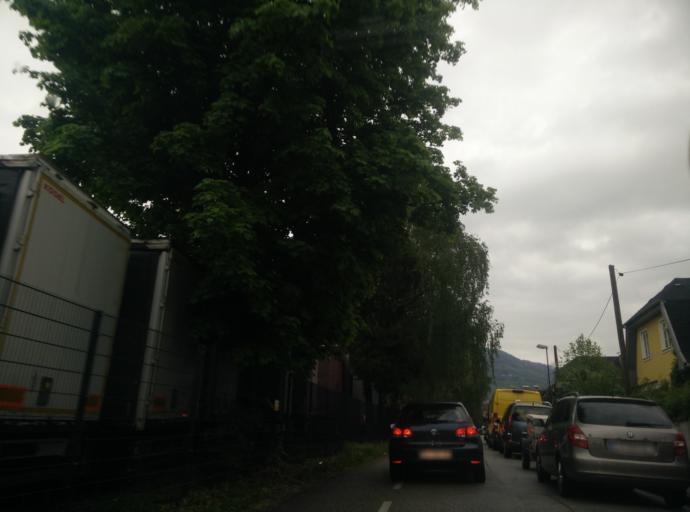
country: AT
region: Salzburg
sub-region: Salzburg Stadt
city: Salzburg
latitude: 47.8131
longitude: 13.0582
